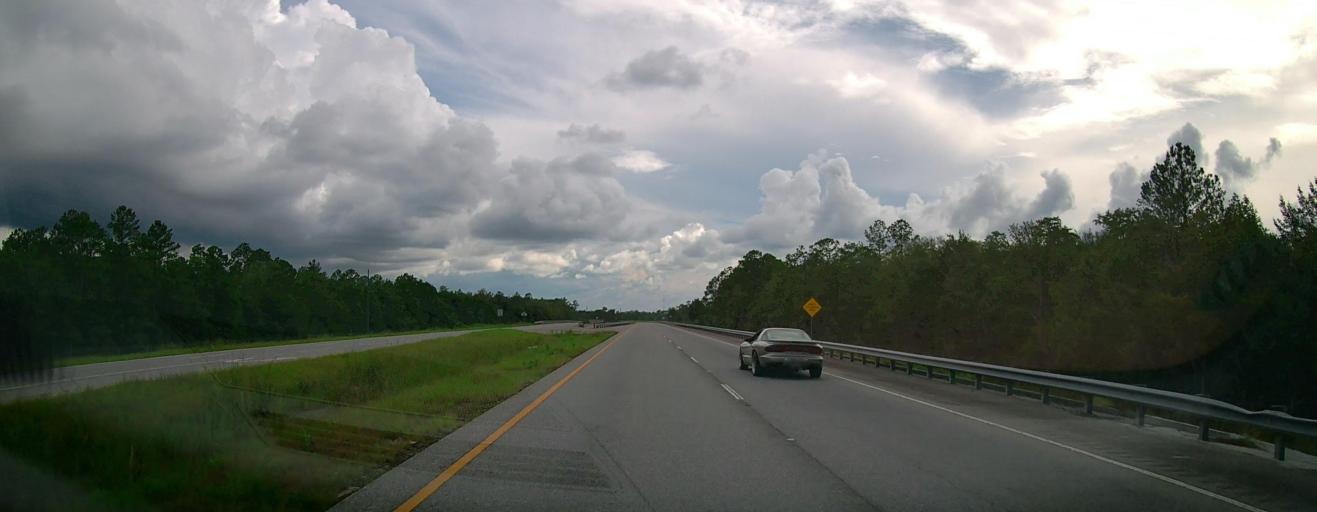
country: US
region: Georgia
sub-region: Wayne County
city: Jesup
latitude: 31.4536
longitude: -82.0606
